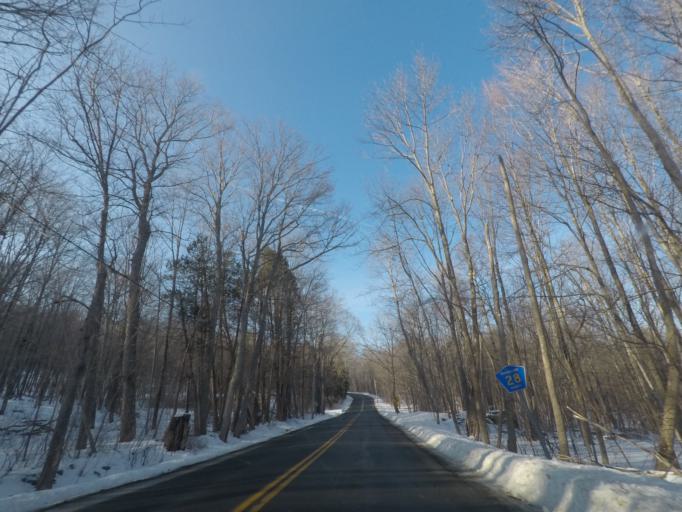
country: US
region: Massachusetts
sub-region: Berkshire County
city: Richmond
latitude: 42.5192
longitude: -73.3764
